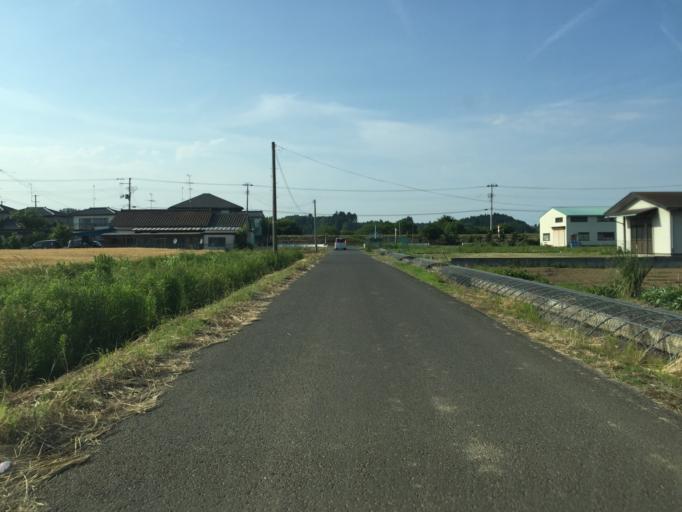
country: JP
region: Miyagi
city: Marumori
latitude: 37.8031
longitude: 140.9486
